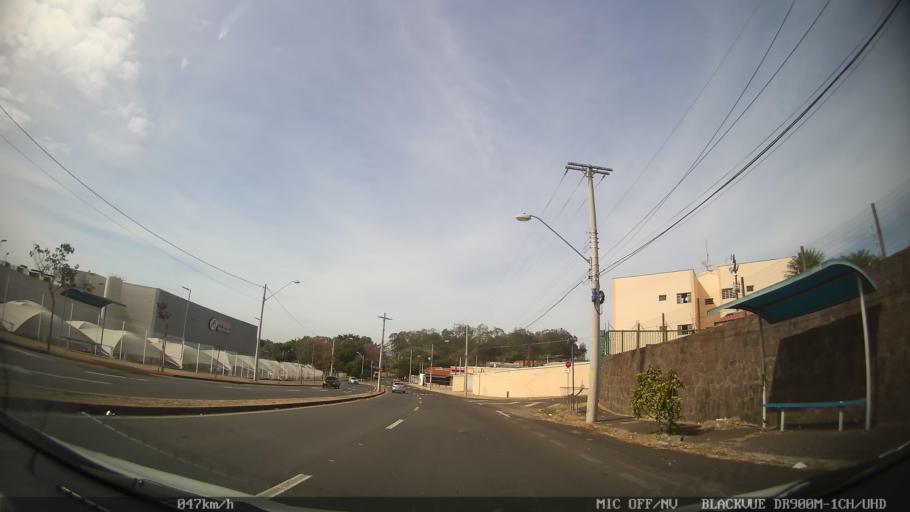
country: BR
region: Sao Paulo
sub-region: Piracicaba
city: Piracicaba
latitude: -22.7475
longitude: -47.6345
